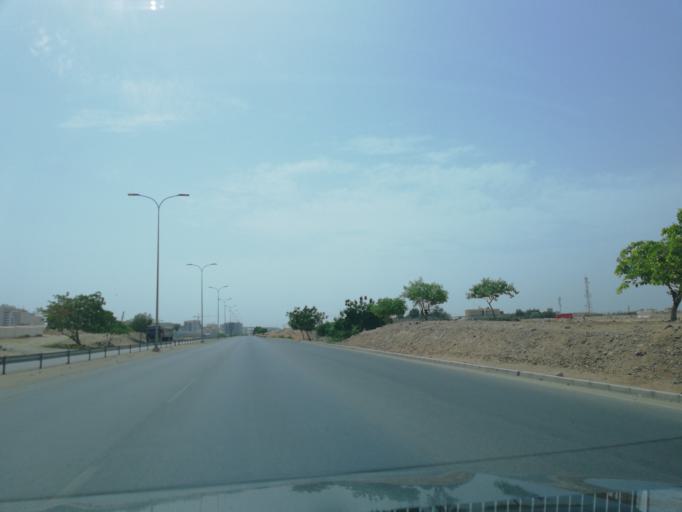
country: OM
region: Muhafazat Masqat
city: Bawshar
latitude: 23.5830
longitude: 58.3518
